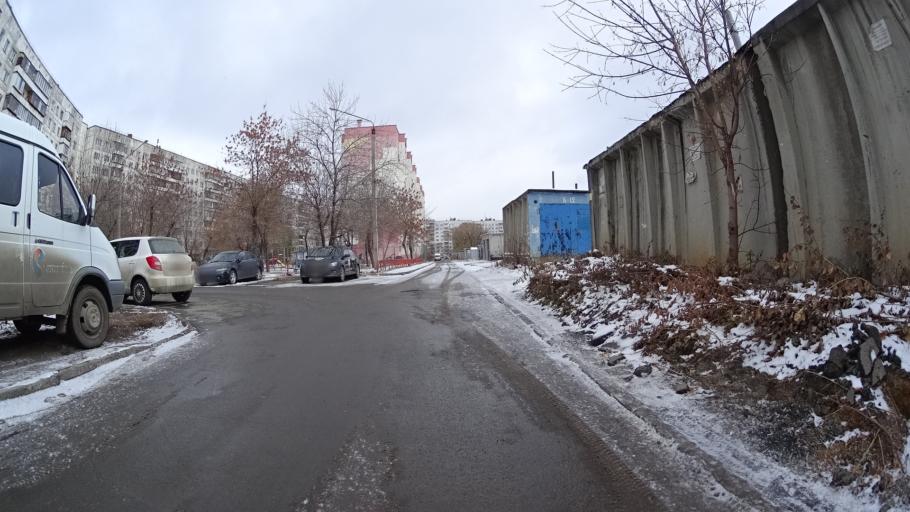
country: RU
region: Chelyabinsk
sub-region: Gorod Chelyabinsk
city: Chelyabinsk
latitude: 55.1878
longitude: 61.3226
